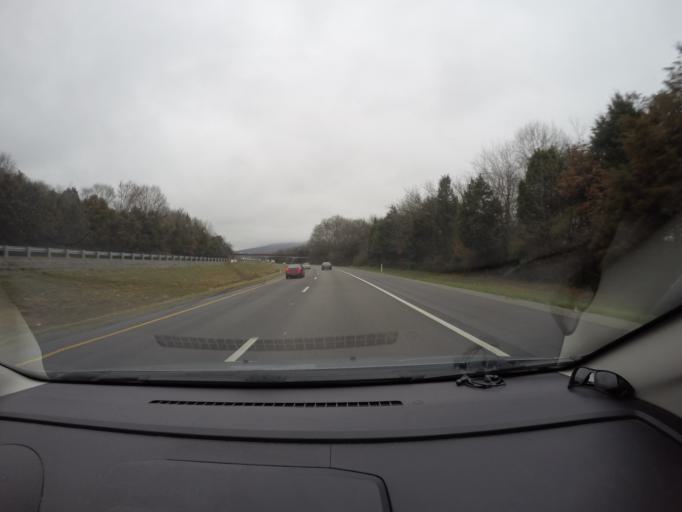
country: US
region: Tennessee
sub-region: Marion County
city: Kimball
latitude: 35.0739
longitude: -85.7360
